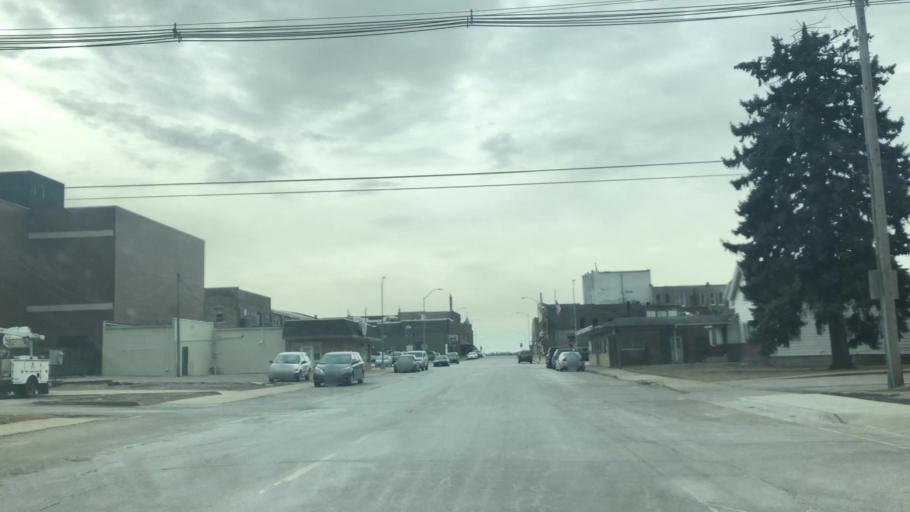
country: US
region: Iowa
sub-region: Marshall County
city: Marshalltown
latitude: 42.0512
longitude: -92.9147
